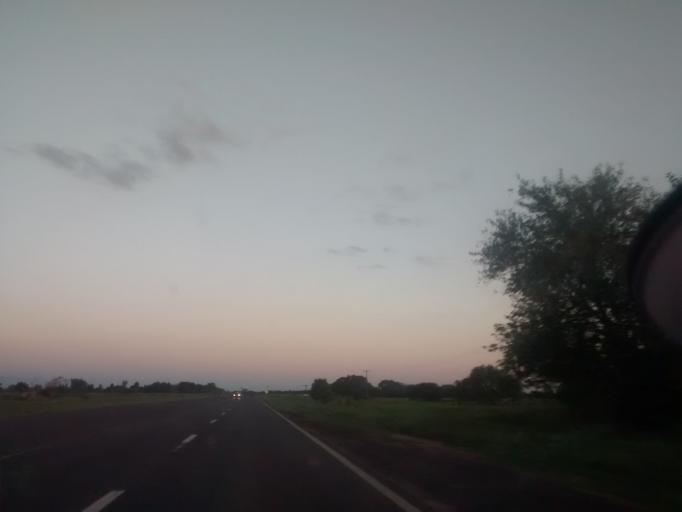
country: AR
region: Chaco
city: Makalle
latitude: -27.1900
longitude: -59.3227
